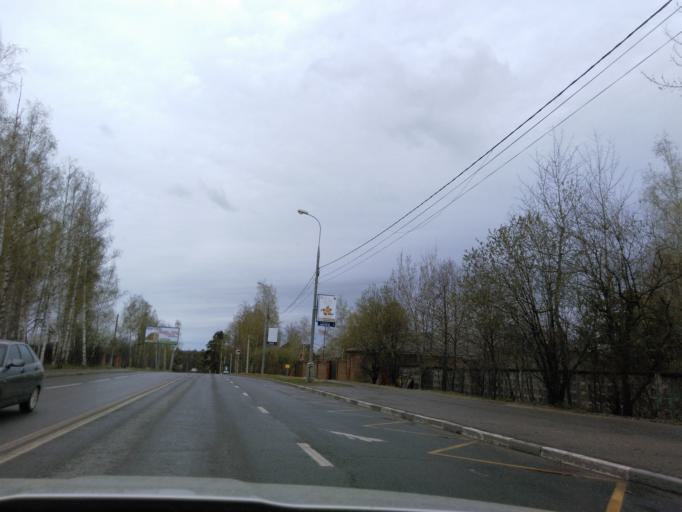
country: RU
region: Moskovskaya
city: Novopodrezkovo
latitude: 55.9073
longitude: 37.3677
